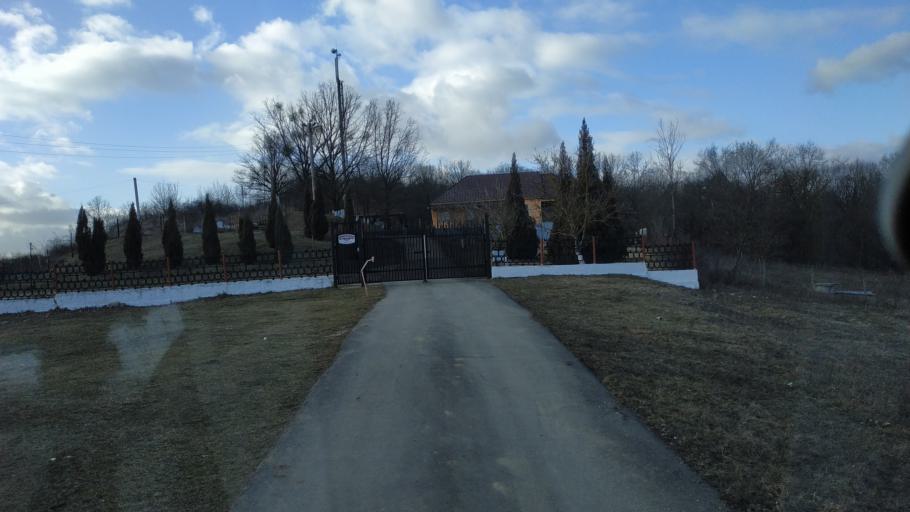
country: MD
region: Calarasi
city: Calarasi
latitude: 47.3318
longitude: 28.0890
